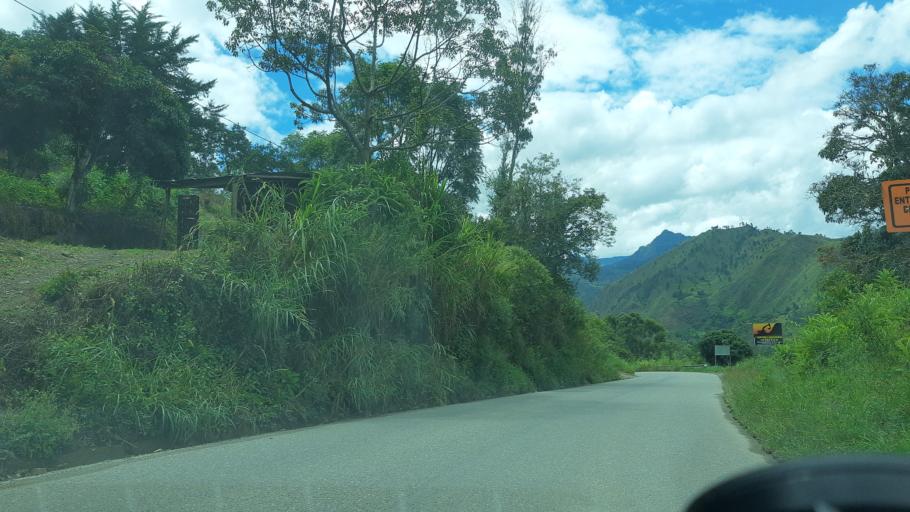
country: CO
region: Boyaca
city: Garagoa
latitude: 5.0432
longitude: -73.3883
